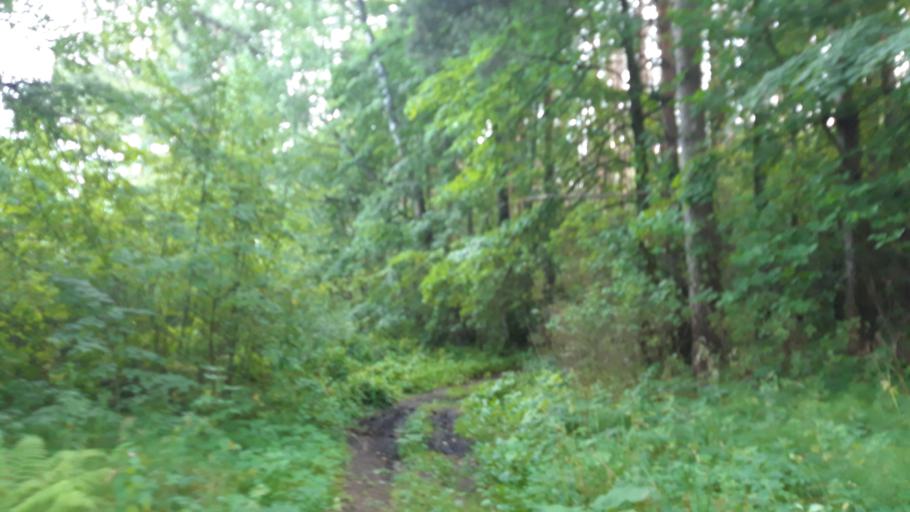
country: RU
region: Tverskaya
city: Konakovo
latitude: 56.6963
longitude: 36.7290
